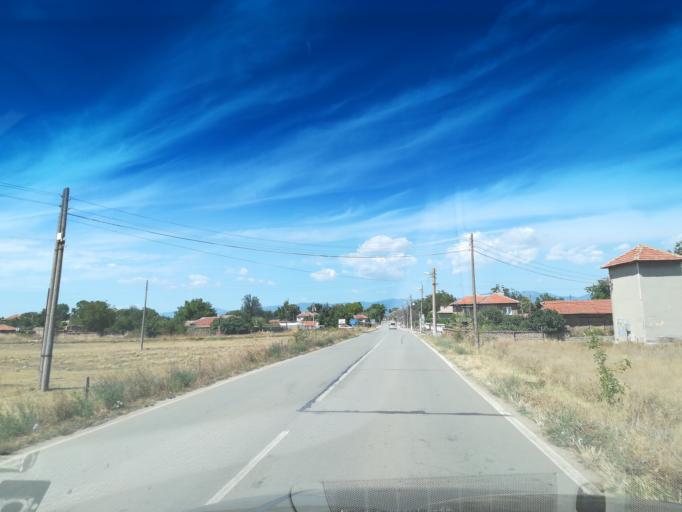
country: BG
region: Plovdiv
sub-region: Obshtina Suedinenie
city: Suedinenie
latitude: 42.3662
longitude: 24.5954
